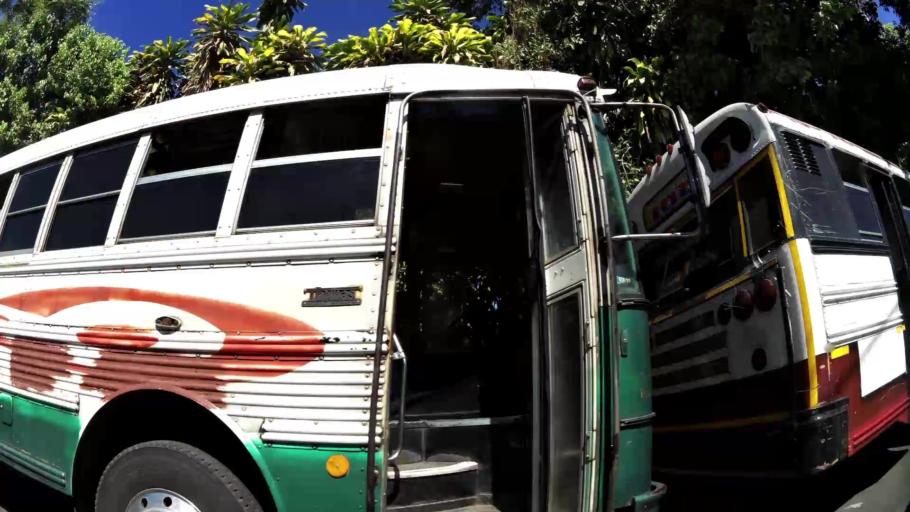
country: SV
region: La Libertad
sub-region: Distrito de Quezaltepeque
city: Quezaltepeque
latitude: 13.8351
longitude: -89.2741
